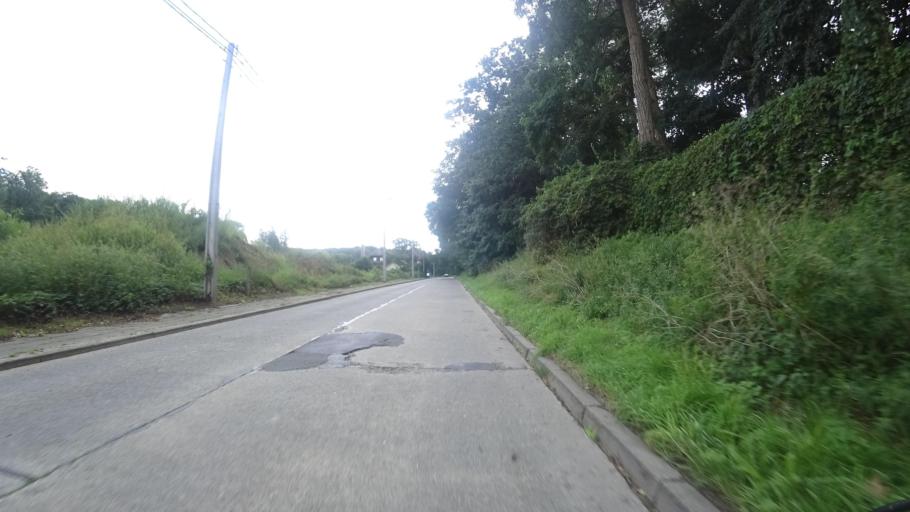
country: BE
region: Wallonia
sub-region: Province du Brabant Wallon
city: Grez-Doiceau
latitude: 50.7601
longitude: 4.6557
